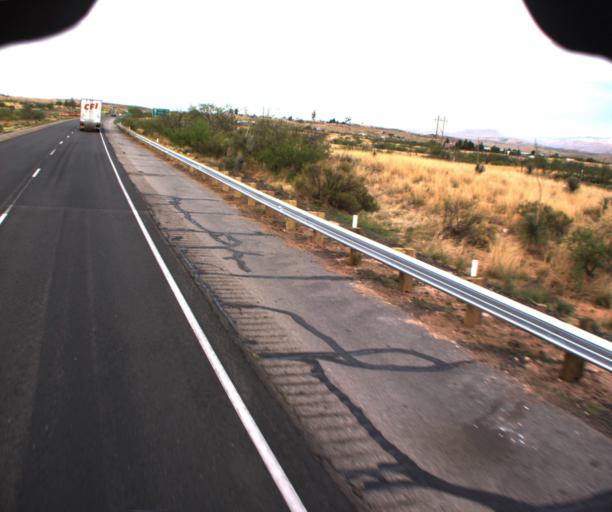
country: US
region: Arizona
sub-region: Cochise County
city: Mescal
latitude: 31.9632
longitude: -110.4480
